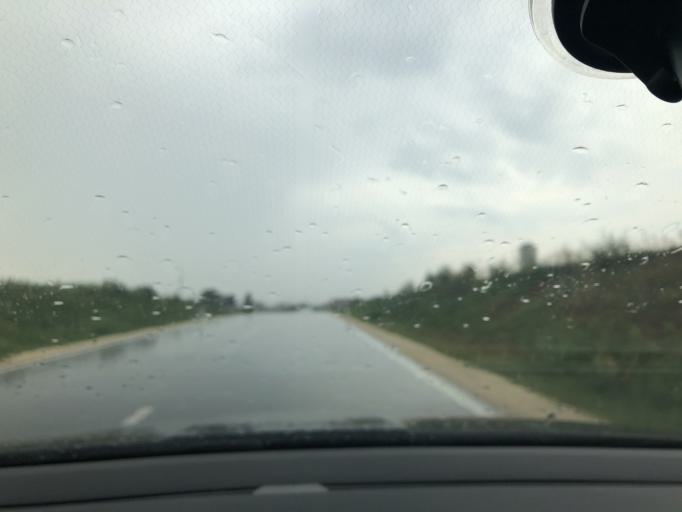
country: AT
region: Lower Austria
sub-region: Politischer Bezirk Ganserndorf
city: Auersthal
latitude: 48.3667
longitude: 16.6492
